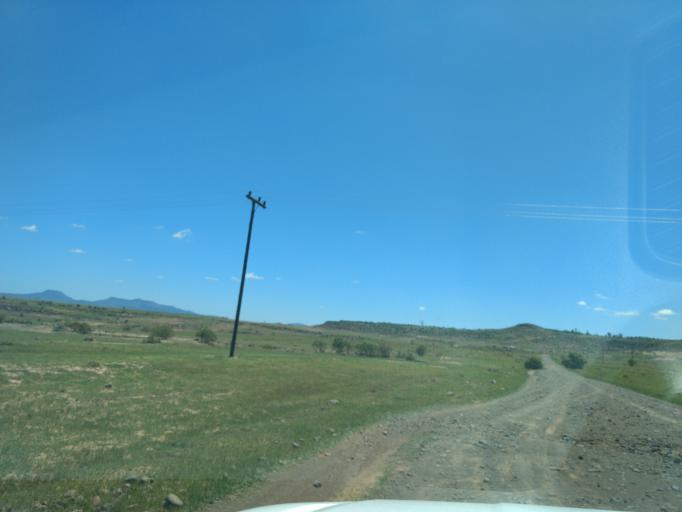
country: LS
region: Maseru
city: Maseru
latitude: -29.4735
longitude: 27.3752
